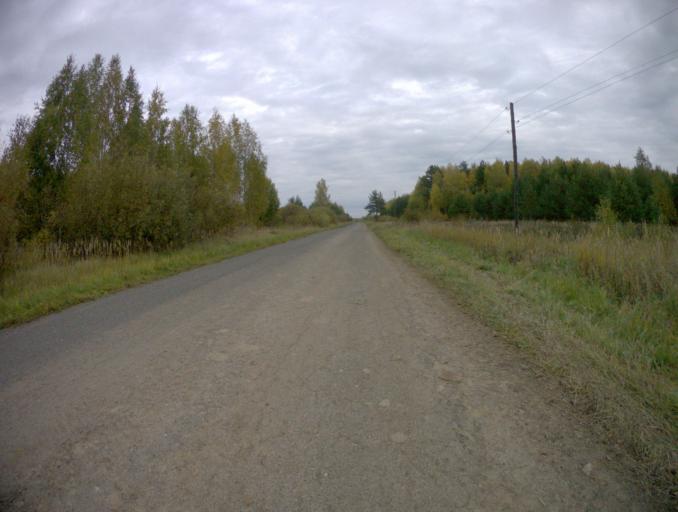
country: RU
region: Vladimir
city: Mstera
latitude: 56.3714
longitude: 41.8157
